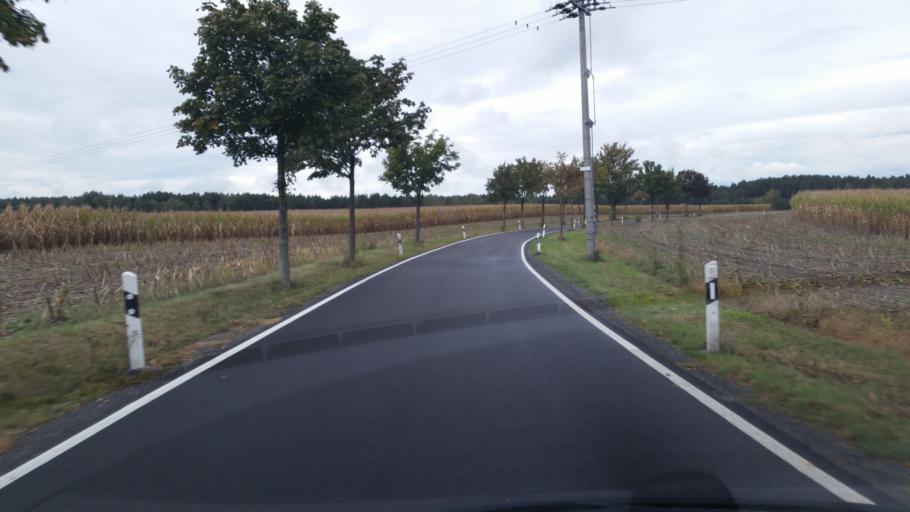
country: DE
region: Saxony
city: Schwepnitz
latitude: 51.3359
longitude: 14.0030
